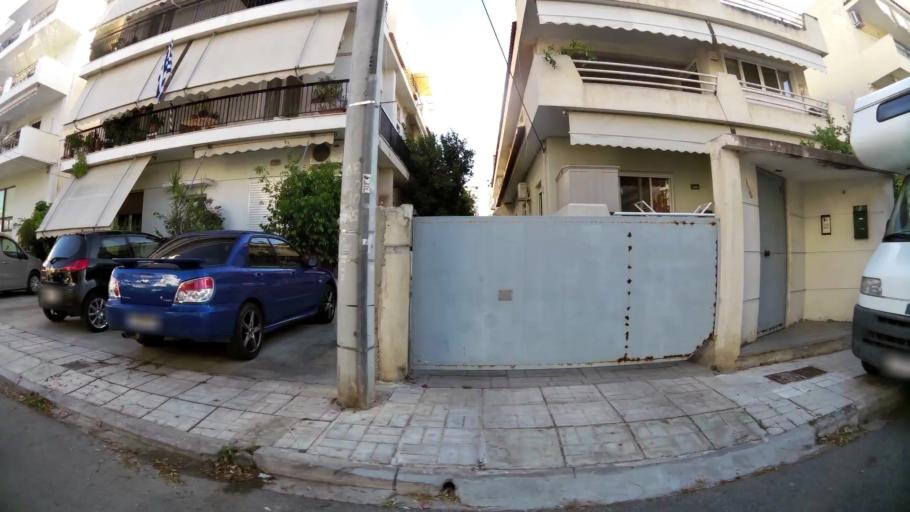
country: GR
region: Attica
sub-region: Nomarchia Athinas
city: Argyroupoli
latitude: 37.8873
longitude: 23.7574
